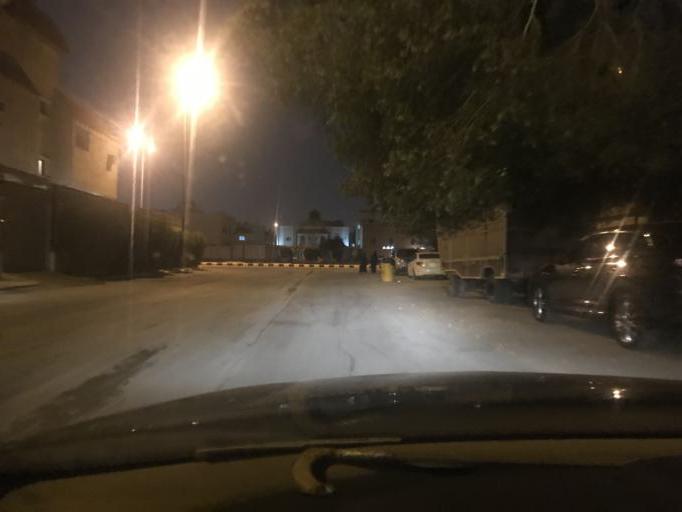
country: SA
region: Ar Riyad
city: Riyadh
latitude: 24.7523
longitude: 46.7769
